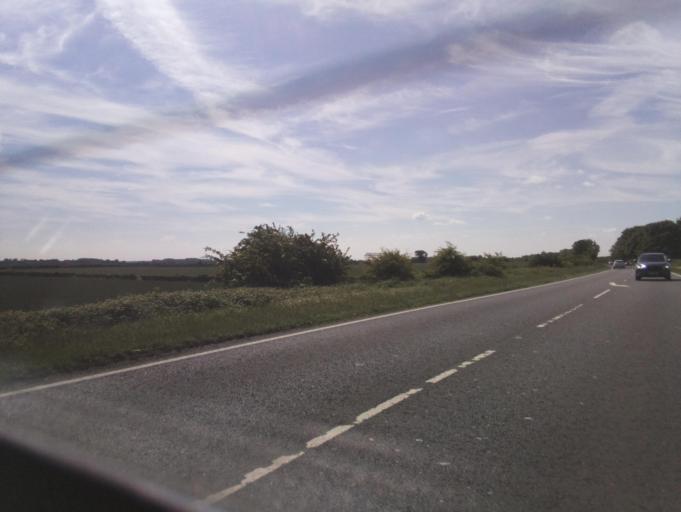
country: GB
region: England
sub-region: Lincolnshire
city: Burton
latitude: 53.3335
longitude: -0.5436
